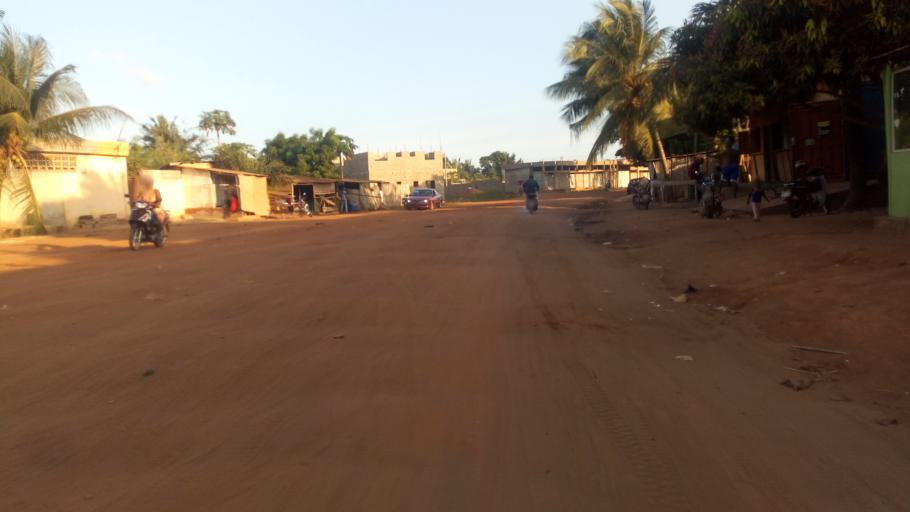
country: TG
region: Maritime
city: Lome
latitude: 6.2198
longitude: 1.1825
